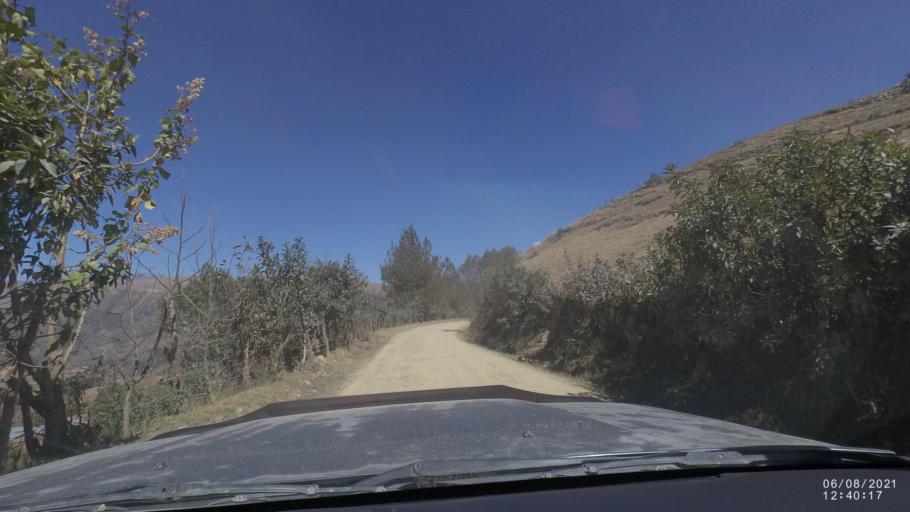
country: BO
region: Cochabamba
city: Colchani
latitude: -16.7830
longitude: -66.6639
